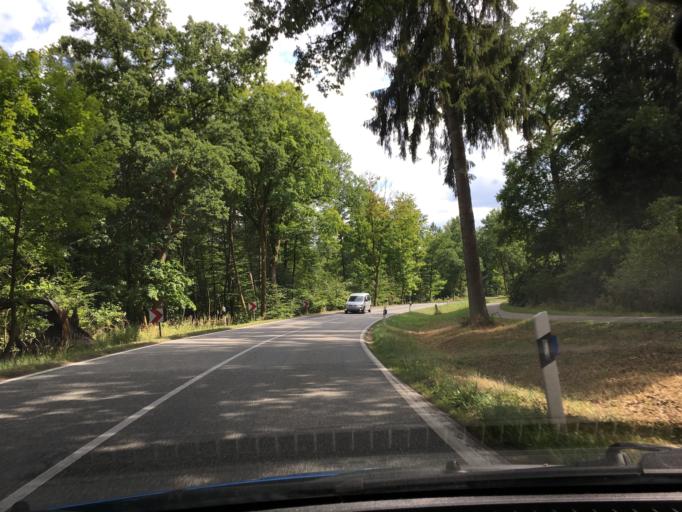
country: DE
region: Mecklenburg-Vorpommern
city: Lubtheen
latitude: 53.3542
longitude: 11.0872
